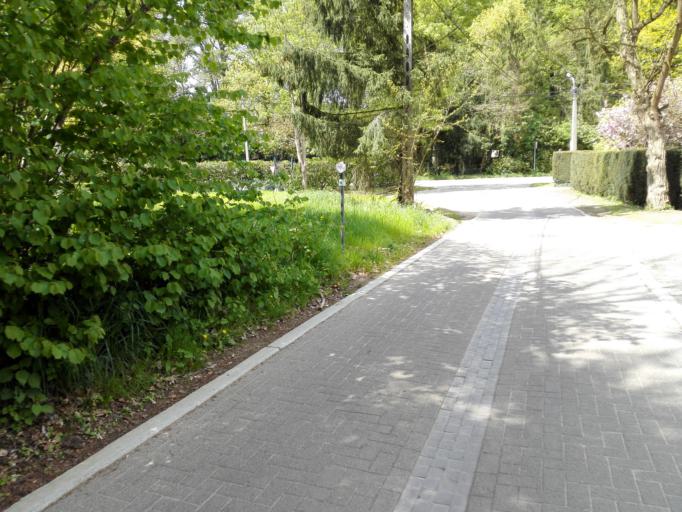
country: BE
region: Flanders
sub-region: Provincie Vlaams-Brabant
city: Rotselaar
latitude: 50.9676
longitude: 4.7432
